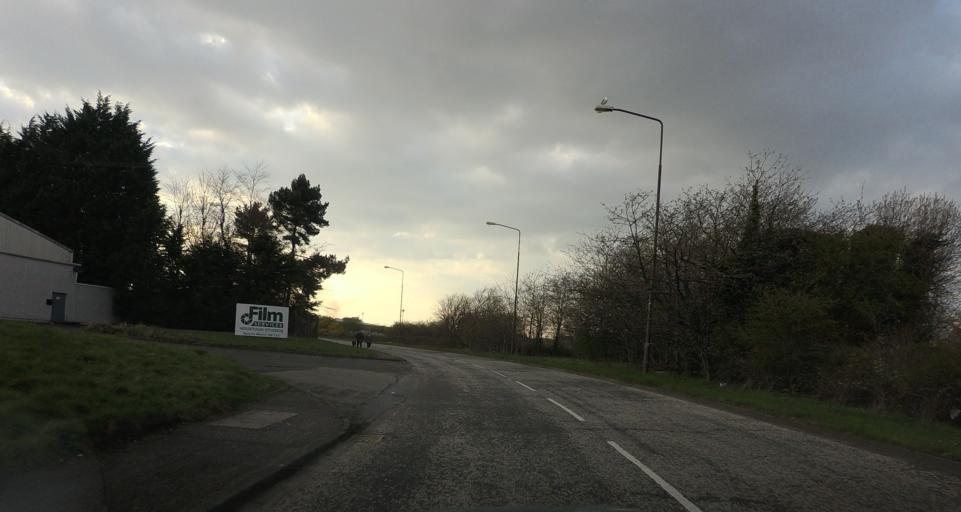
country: GB
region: Scotland
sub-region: West Lothian
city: Livingston
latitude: 55.9132
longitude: -3.5009
